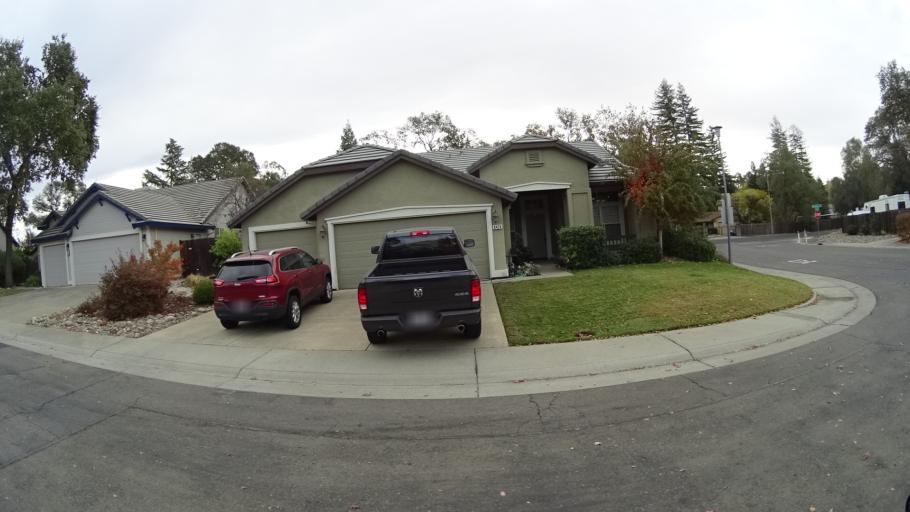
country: US
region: California
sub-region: Sacramento County
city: Citrus Heights
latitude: 38.7170
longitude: -121.2450
